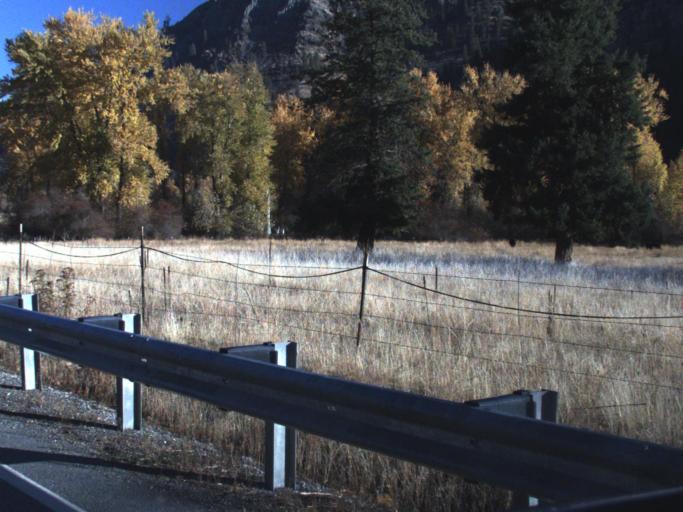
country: US
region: Washington
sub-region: Ferry County
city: Republic
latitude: 48.3015
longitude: -118.7355
